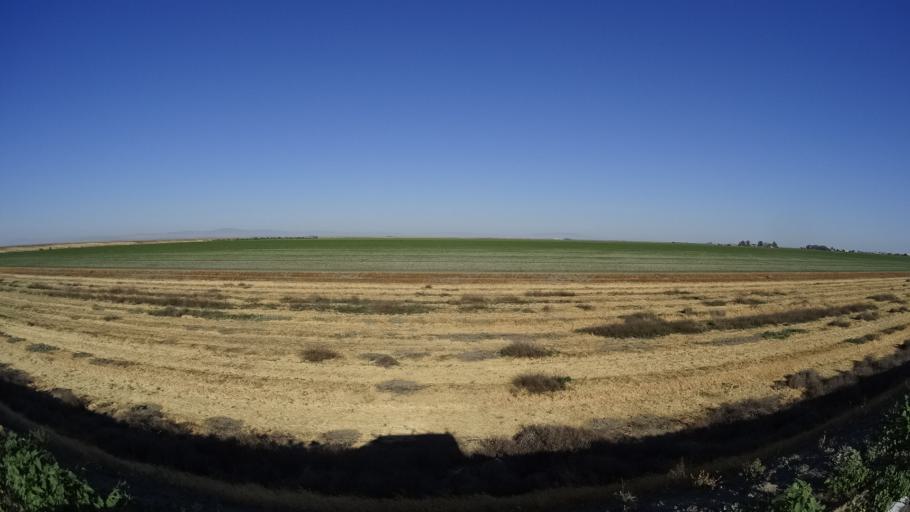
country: US
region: California
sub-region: Kings County
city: Stratford
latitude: 36.1423
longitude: -119.7981
